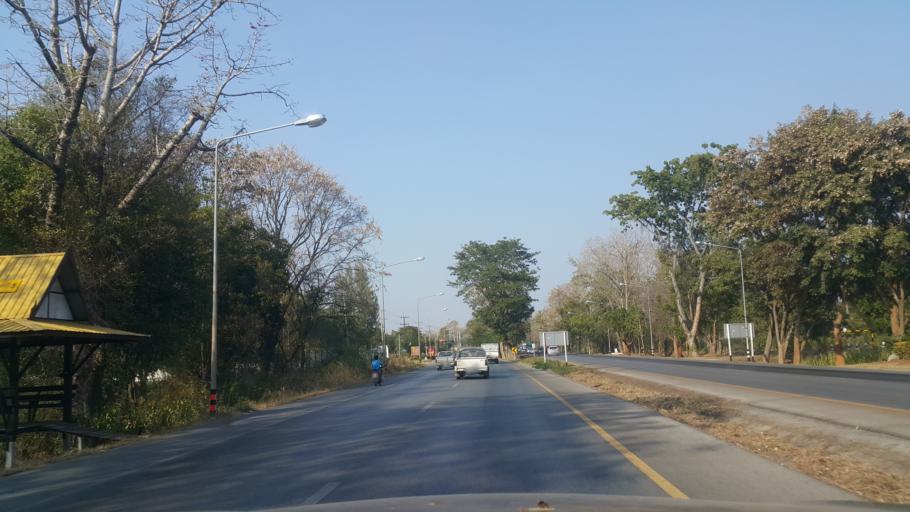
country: TH
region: Nakhon Ratchasima
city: Nakhon Ratchasima
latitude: 14.8639
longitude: 102.0707
